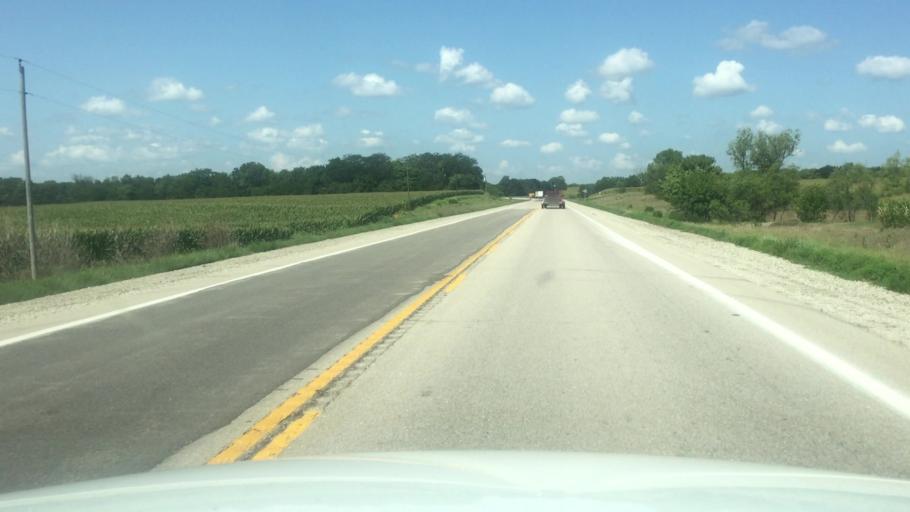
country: US
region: Kansas
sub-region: Brown County
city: Hiawatha
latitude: 39.8484
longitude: -95.6635
